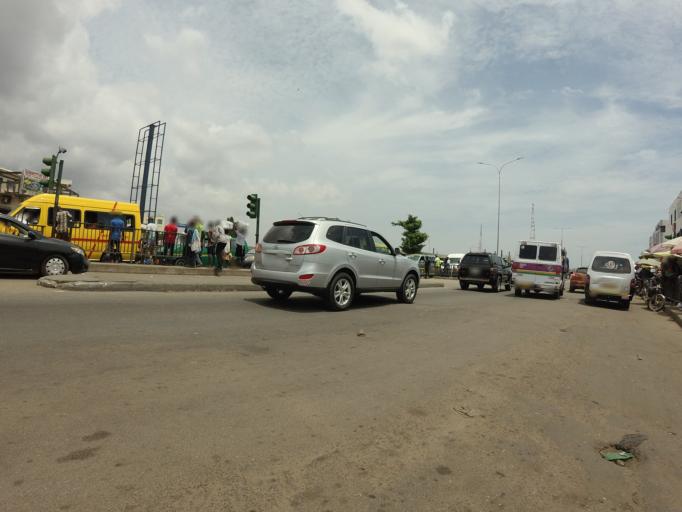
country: GH
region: Greater Accra
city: Accra
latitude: 5.5630
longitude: -0.2324
